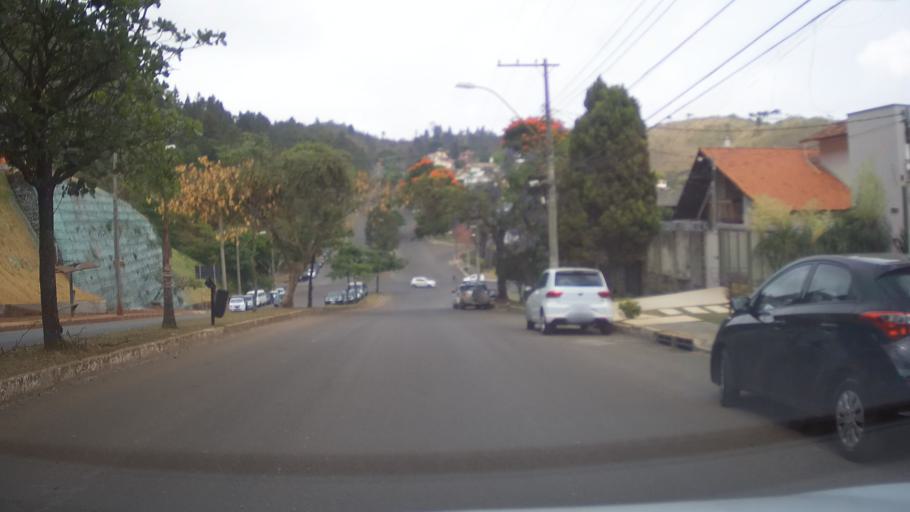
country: BR
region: Minas Gerais
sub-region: Belo Horizonte
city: Belo Horizonte
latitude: -19.9584
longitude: -43.9132
